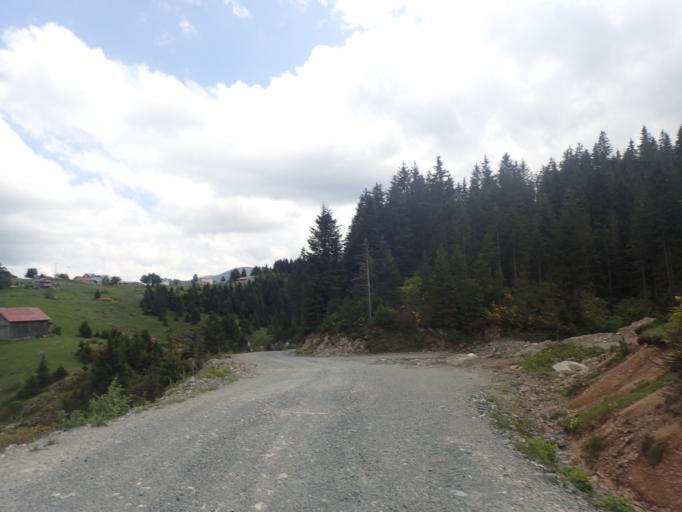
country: TR
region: Ordu
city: Topcam
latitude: 40.6828
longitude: 37.9439
